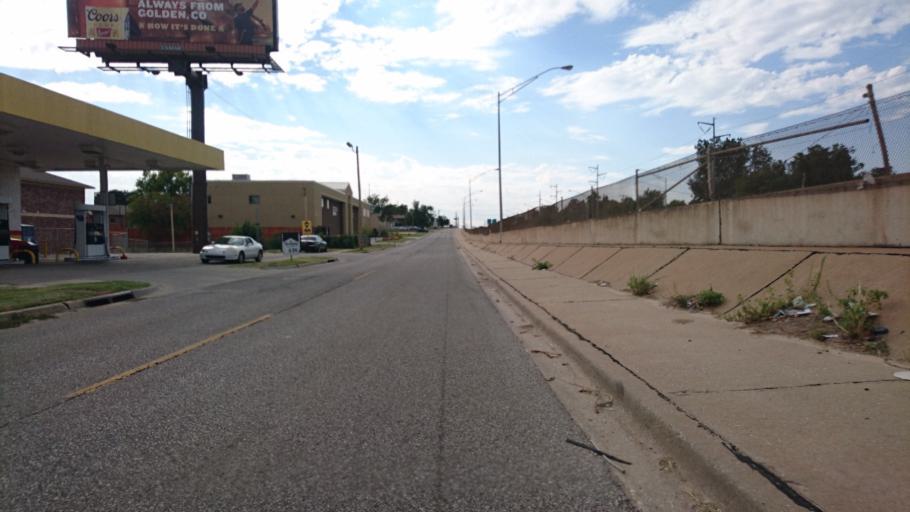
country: US
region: Oklahoma
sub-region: Oklahoma County
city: Nichols Hills
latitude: 35.5113
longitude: -97.5558
